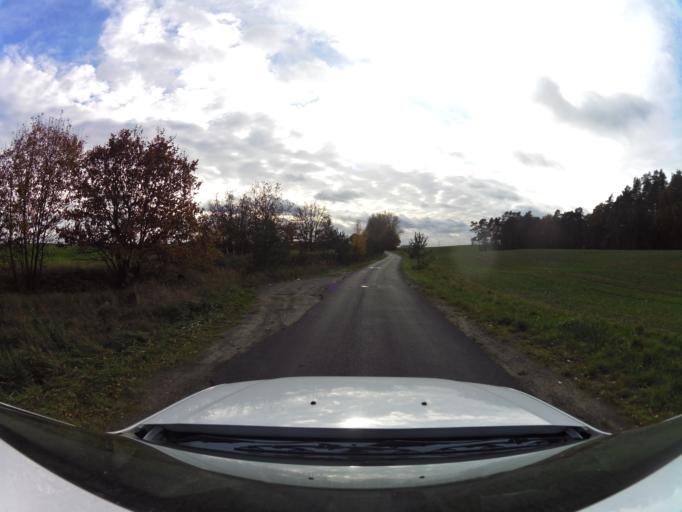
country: PL
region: West Pomeranian Voivodeship
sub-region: Powiat gryficki
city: Gryfice
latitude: 53.9039
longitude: 15.1341
